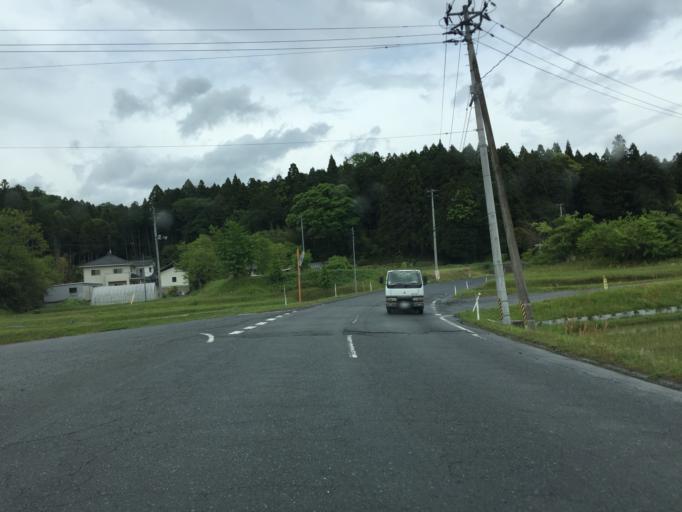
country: JP
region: Ibaraki
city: Kitaibaraki
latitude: 36.9473
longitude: 140.7507
